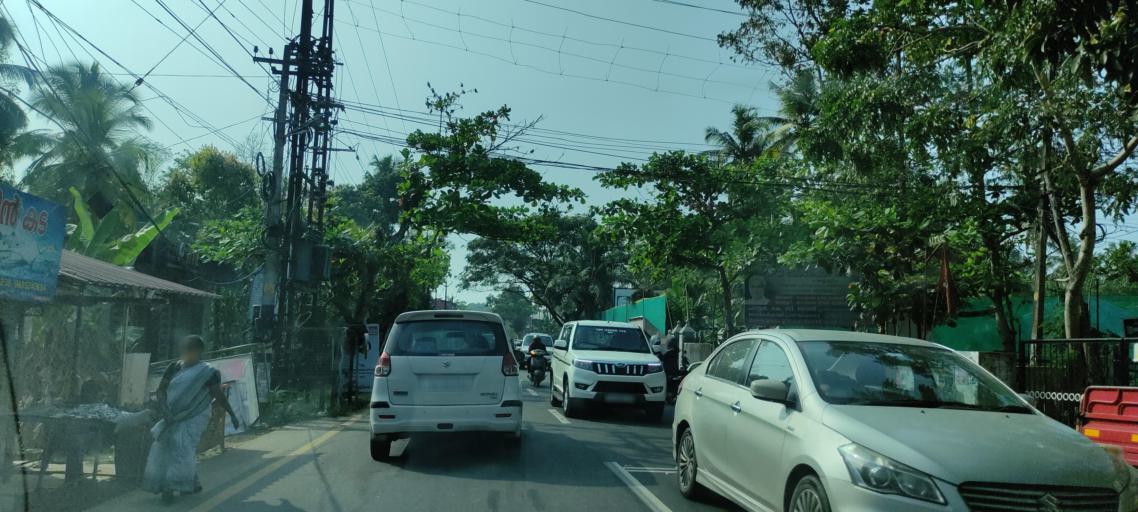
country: IN
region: Kerala
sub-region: Pattanamtitta
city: Tiruvalla
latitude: 9.3712
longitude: 76.5204
